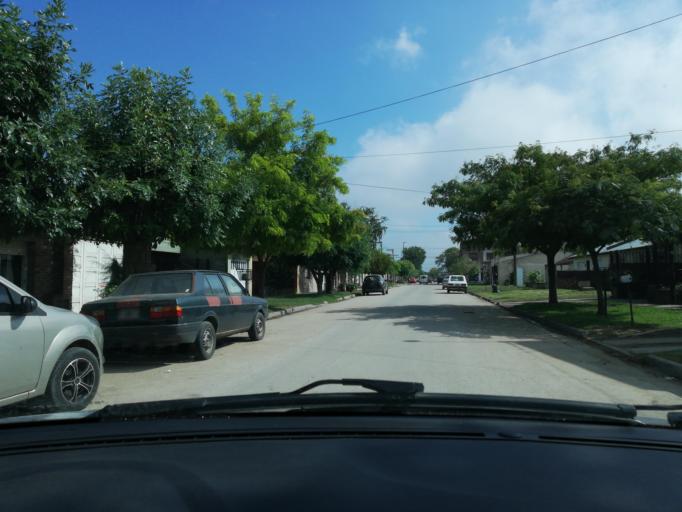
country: AR
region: Buenos Aires
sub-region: Partido de Balcarce
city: Balcarce
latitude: -37.8484
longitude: -58.2432
